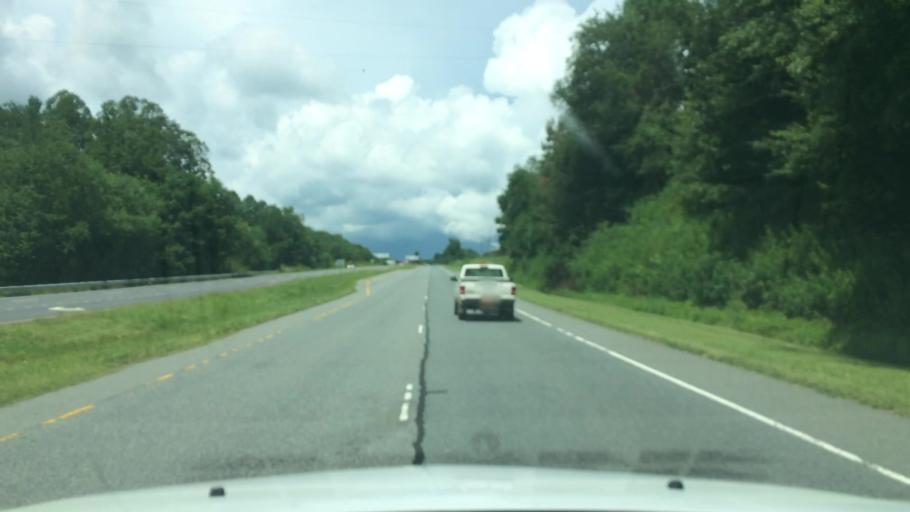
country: US
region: North Carolina
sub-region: Wilkes County
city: Millers Creek
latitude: 36.1449
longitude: -81.3041
